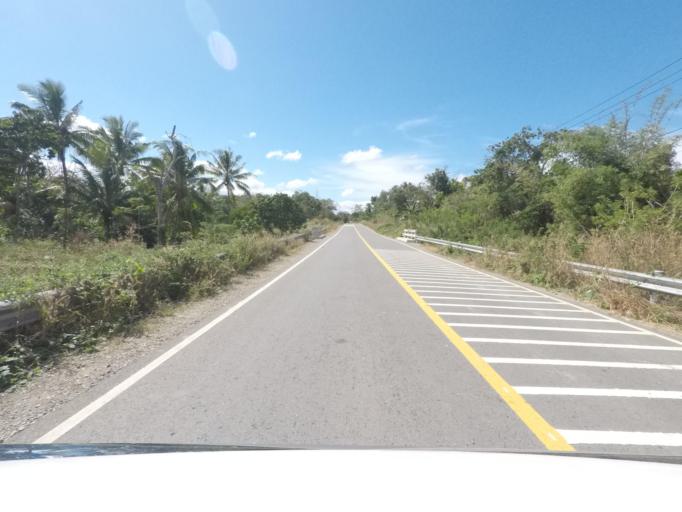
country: TL
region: Baucau
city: Baucau
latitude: -8.4908
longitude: 126.3612
